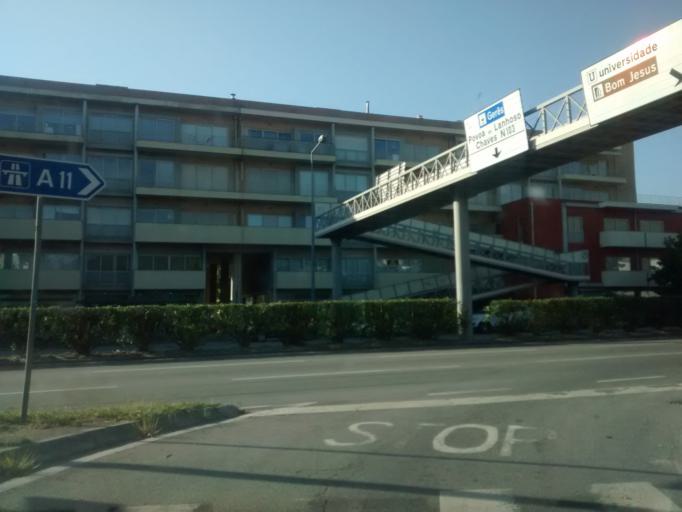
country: PT
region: Braga
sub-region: Braga
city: Braga
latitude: 41.5549
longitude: -8.4009
